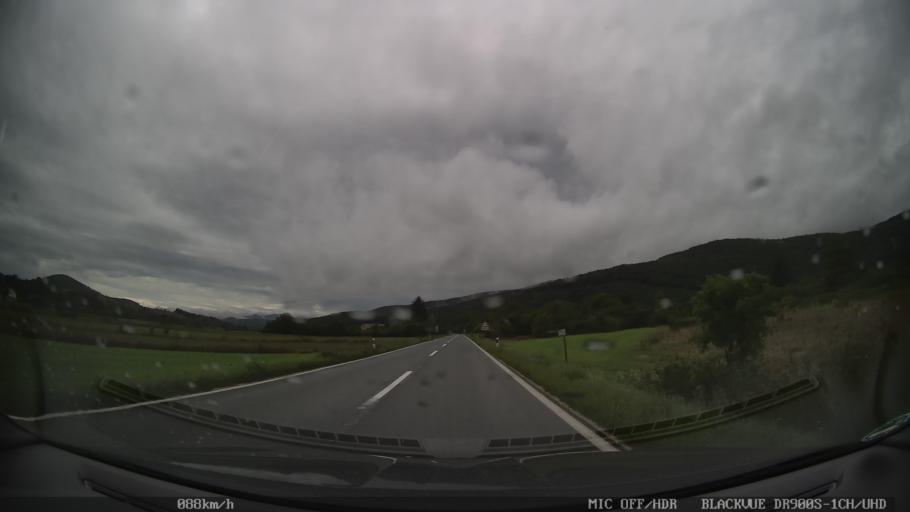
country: HR
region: Licko-Senjska
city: Brinje
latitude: 44.9440
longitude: 15.1259
